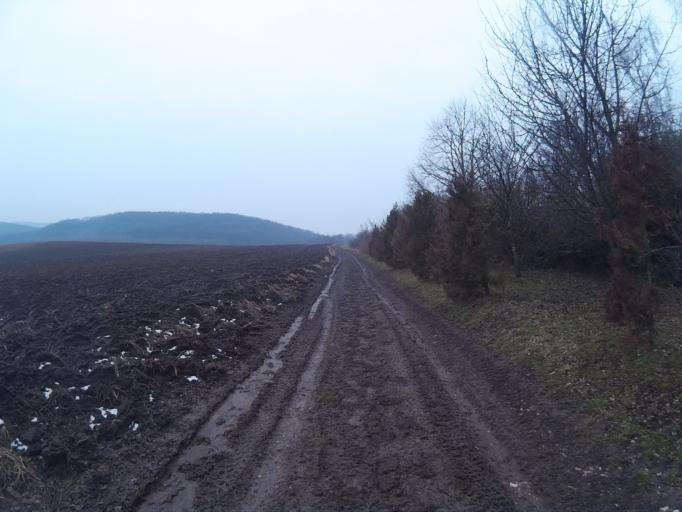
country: HU
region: Komarom-Esztergom
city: Tarjan
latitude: 47.6022
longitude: 18.5152
